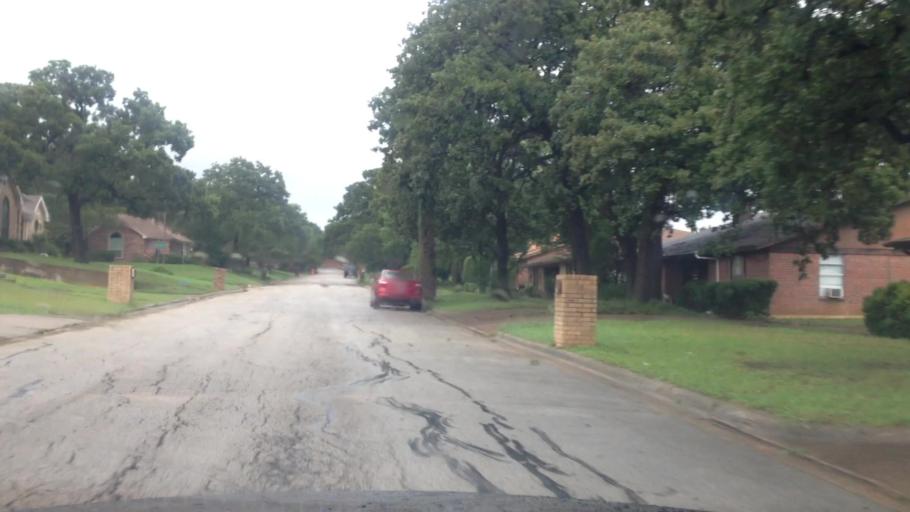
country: US
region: Texas
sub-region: Tarrant County
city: Watauga
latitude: 32.8841
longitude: -97.2290
